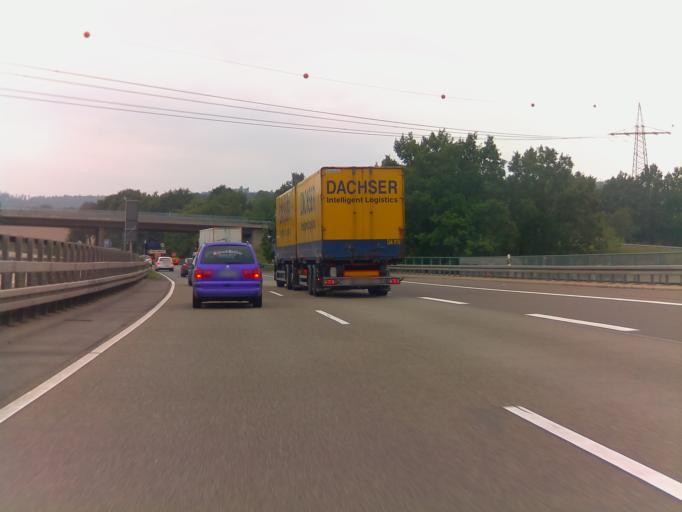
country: DE
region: Hesse
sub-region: Regierungsbezirk Kassel
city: Niederaula
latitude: 50.7757
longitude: 9.5857
